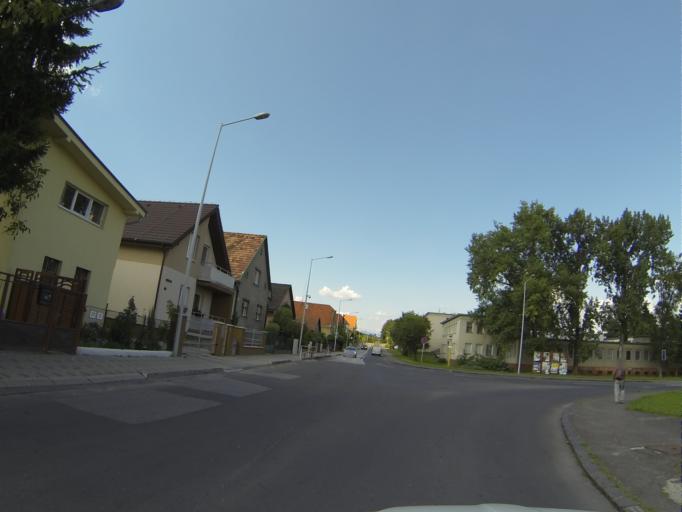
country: SK
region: Nitriansky
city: Bojnice
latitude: 48.7855
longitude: 18.5861
